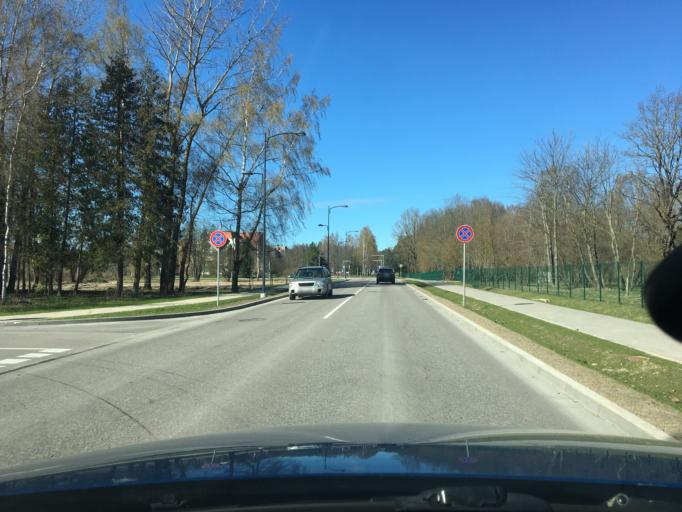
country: LV
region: Salaspils
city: Salaspils
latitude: 56.8671
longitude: 24.3520
